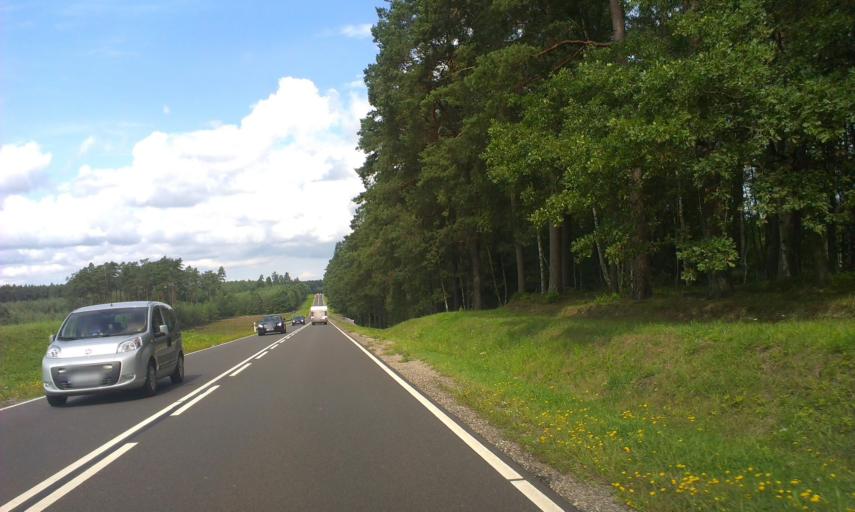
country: PL
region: West Pomeranian Voivodeship
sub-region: Powiat koszalinski
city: Bobolice
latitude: 54.0600
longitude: 16.4139
